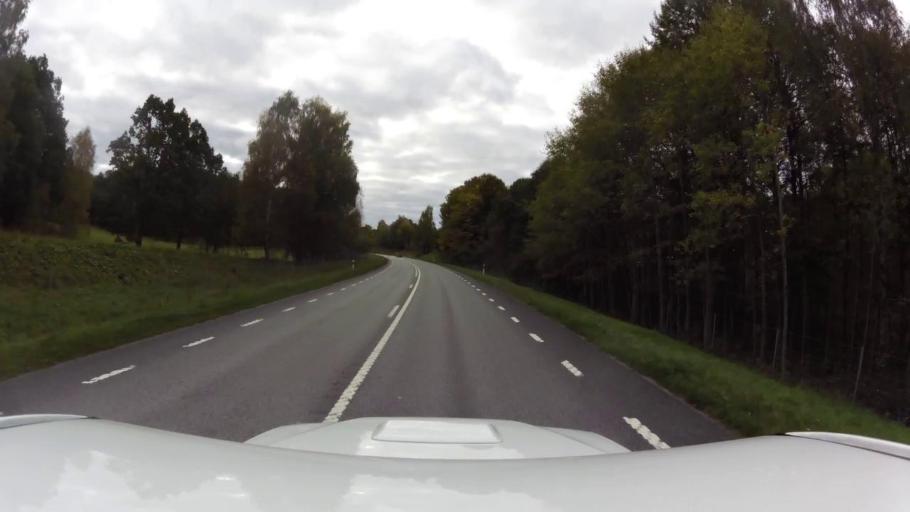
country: SE
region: OEstergoetland
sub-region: Kinda Kommun
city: Rimforsa
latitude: 58.1880
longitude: 15.6667
